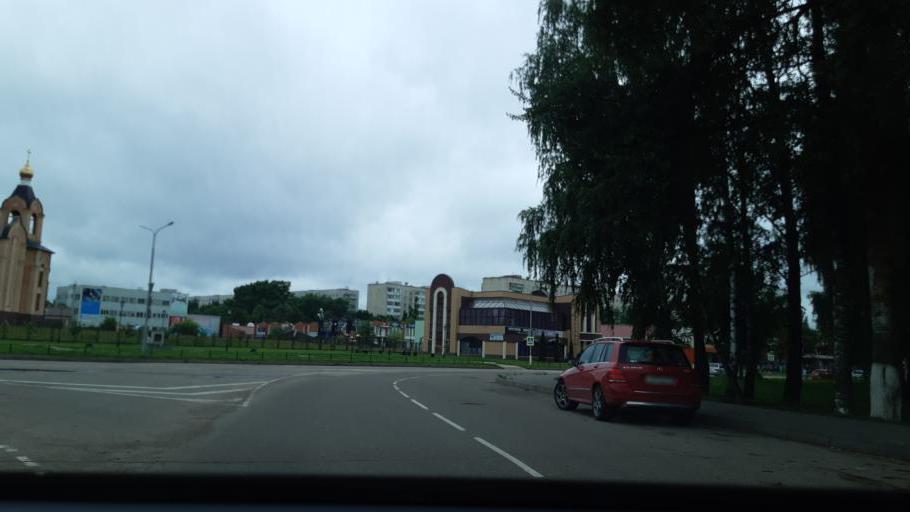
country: RU
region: Smolensk
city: Desnogorsk
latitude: 54.1526
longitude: 33.2882
